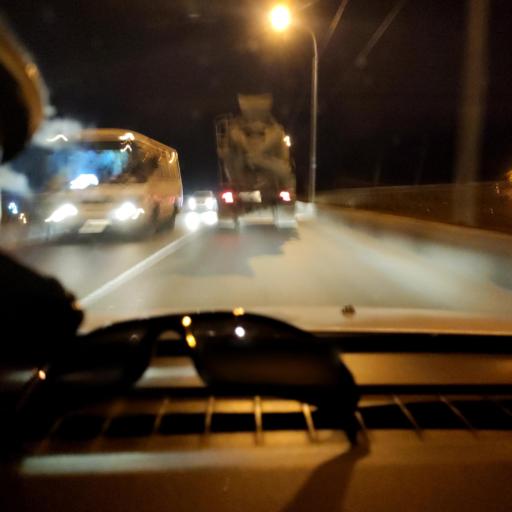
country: RU
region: Samara
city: Novokuybyshevsk
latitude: 53.1164
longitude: 50.0611
